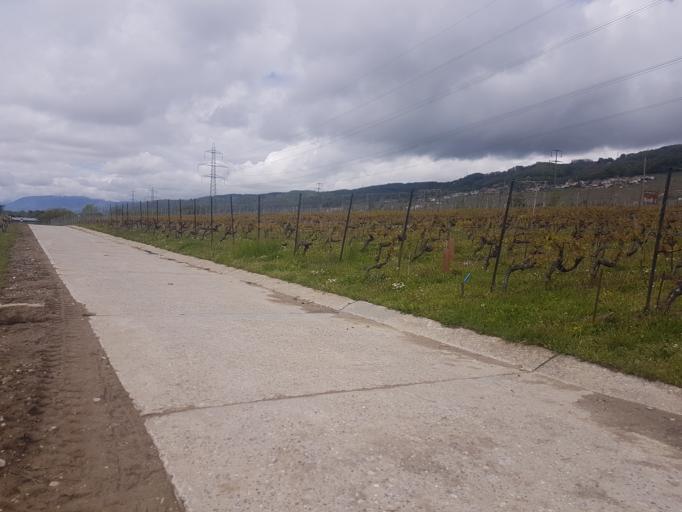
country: CH
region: Vaud
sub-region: Nyon District
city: Perroy
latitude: 46.4698
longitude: 6.3530
